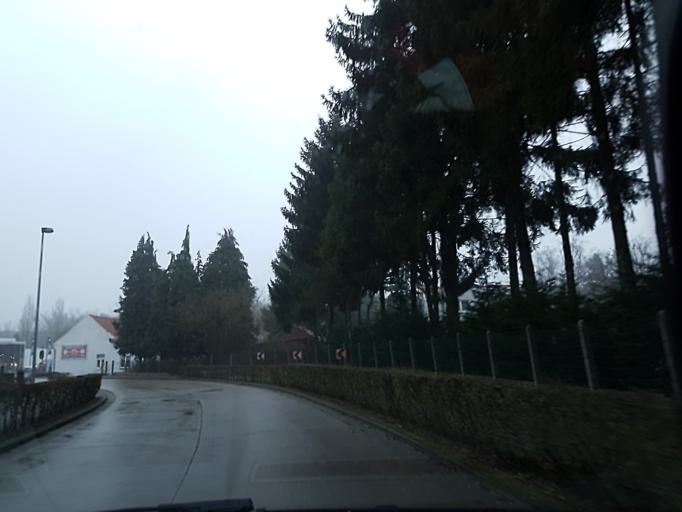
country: BE
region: Flanders
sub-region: Provincie Vlaams-Brabant
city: Boortmeerbeek
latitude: 51.0111
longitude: 4.5873
